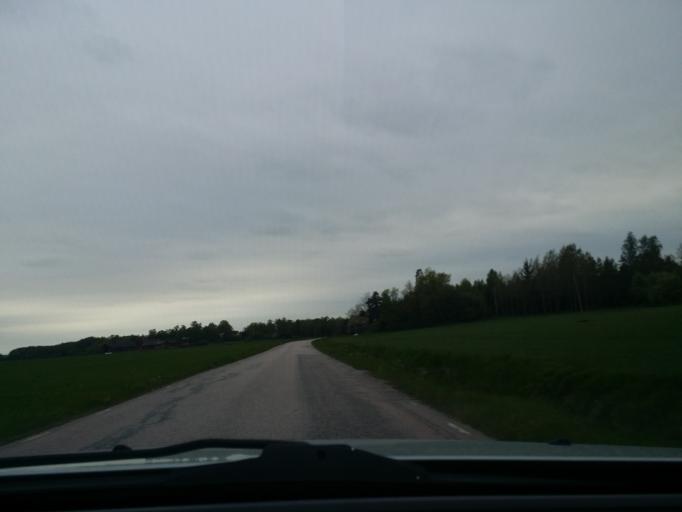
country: SE
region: Vaestmanland
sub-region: Hallstahammars Kommun
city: Kolback
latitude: 59.5477
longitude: 16.3254
